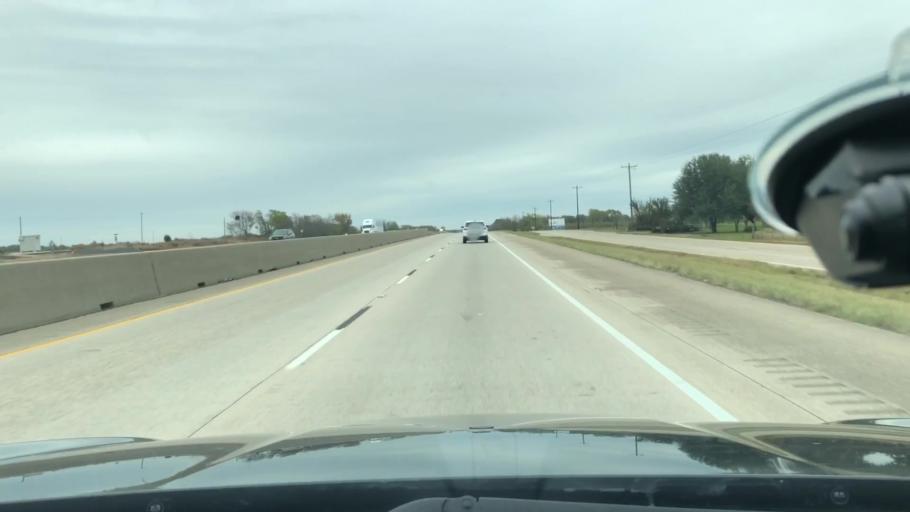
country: US
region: Texas
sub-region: Hunt County
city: Commerce
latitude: 33.1306
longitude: -95.7807
